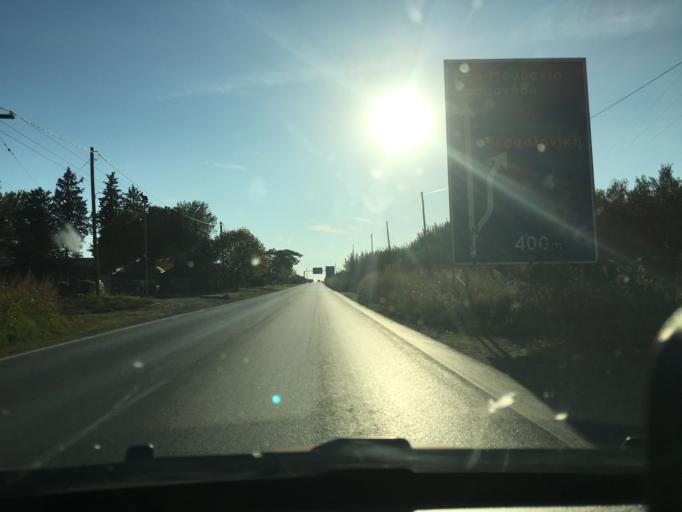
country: GR
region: Central Macedonia
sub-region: Nomos Chalkidikis
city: Nea Moudhania
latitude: 40.2487
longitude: 23.3107
